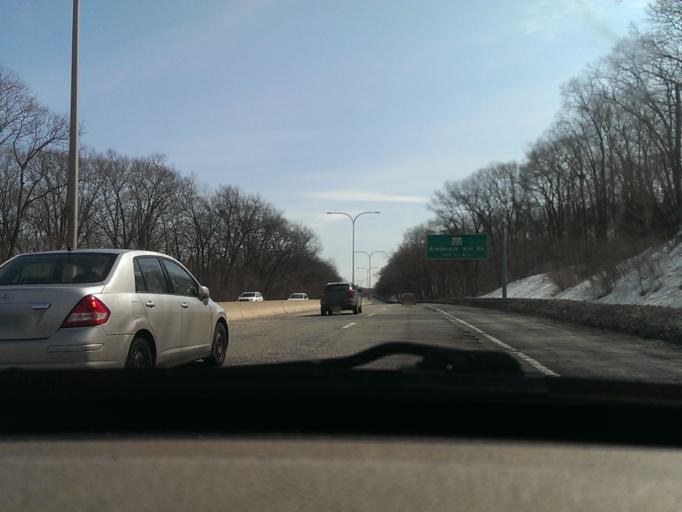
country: US
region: Rhode Island
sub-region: Providence County
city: Cumberland
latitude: 41.9119
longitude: -71.4520
